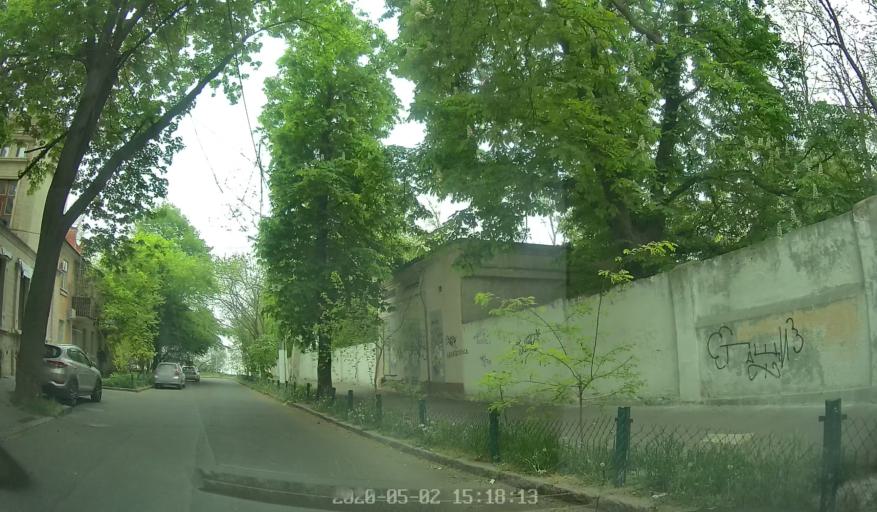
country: GR
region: South Aegean
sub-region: Nomos Kykladon
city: Serifos
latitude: 37.1776
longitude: 24.6072
